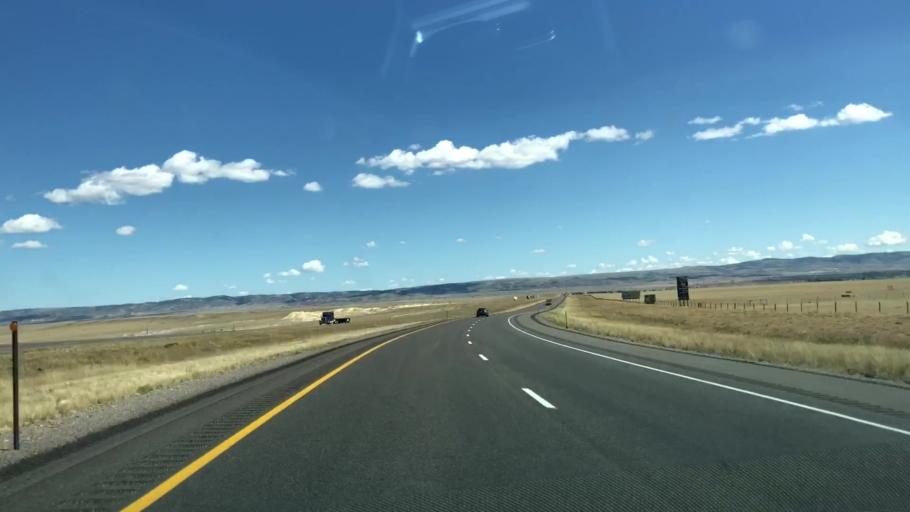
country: US
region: Wyoming
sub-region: Albany County
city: Laramie
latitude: 41.3504
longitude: -105.6971
